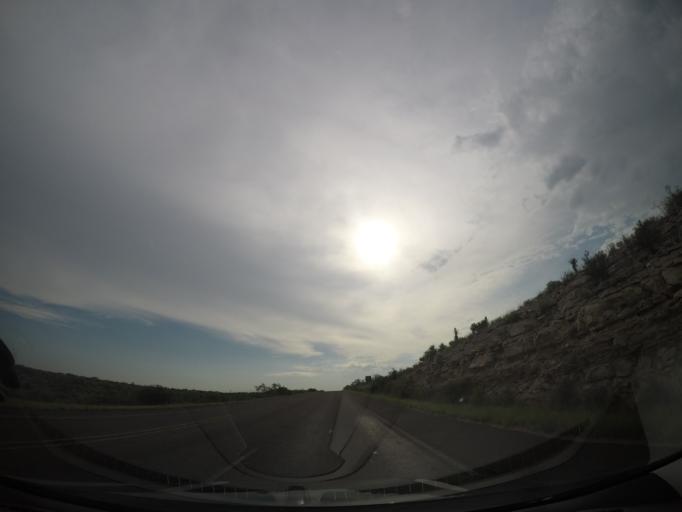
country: US
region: Texas
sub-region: Terrell County
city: Sanderson
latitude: 29.9051
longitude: -101.7750
